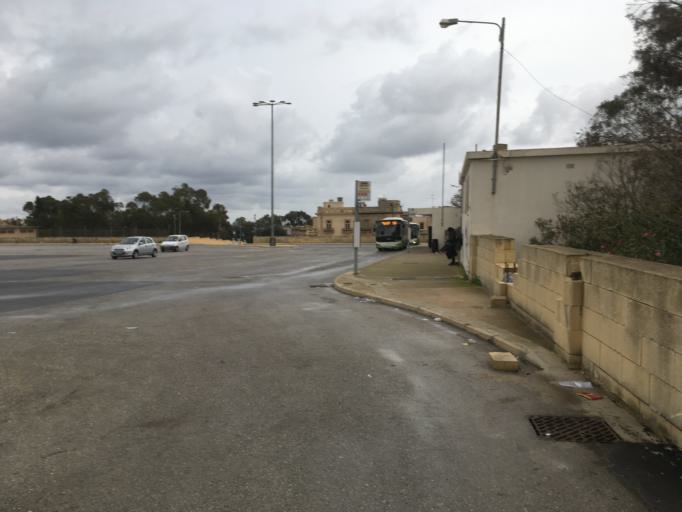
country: MT
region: Is-Swieqi
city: Swieqi
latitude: 35.9239
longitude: 14.4780
